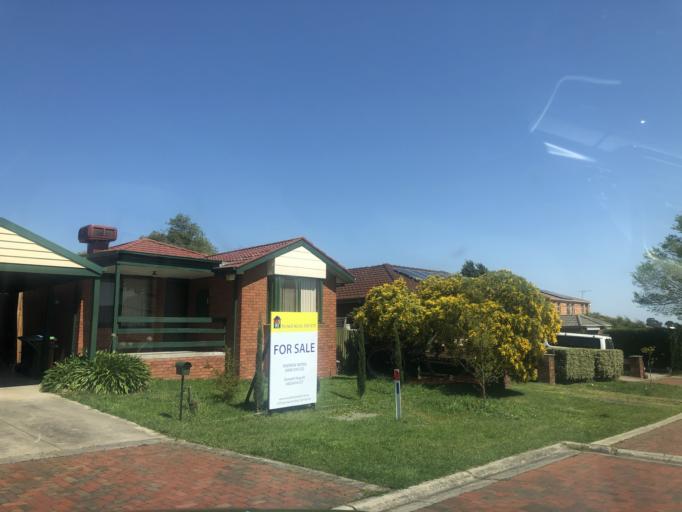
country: AU
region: Victoria
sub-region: Casey
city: Narre Warren South
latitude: -38.0387
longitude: 145.2781
